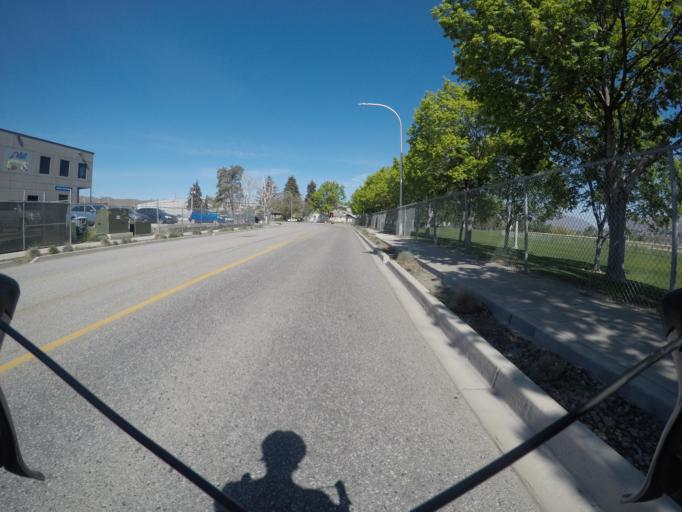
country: US
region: Washington
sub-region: Chelan County
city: Wenatchee
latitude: 47.4445
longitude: -120.3219
